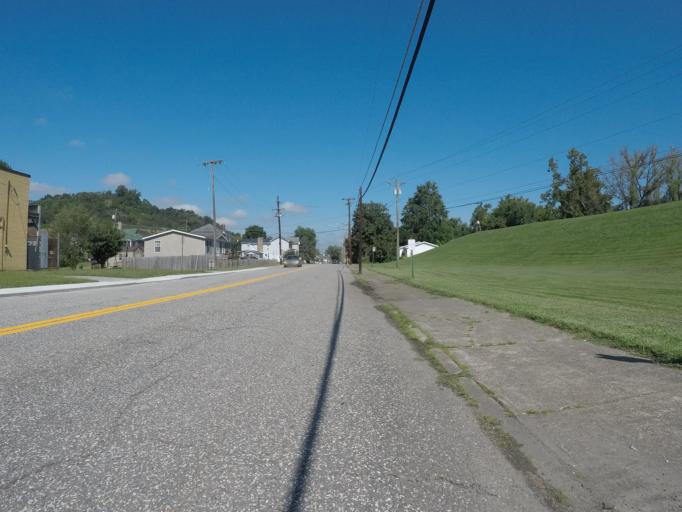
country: US
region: Ohio
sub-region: Lawrence County
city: South Point
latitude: 38.4198
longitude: -82.5984
